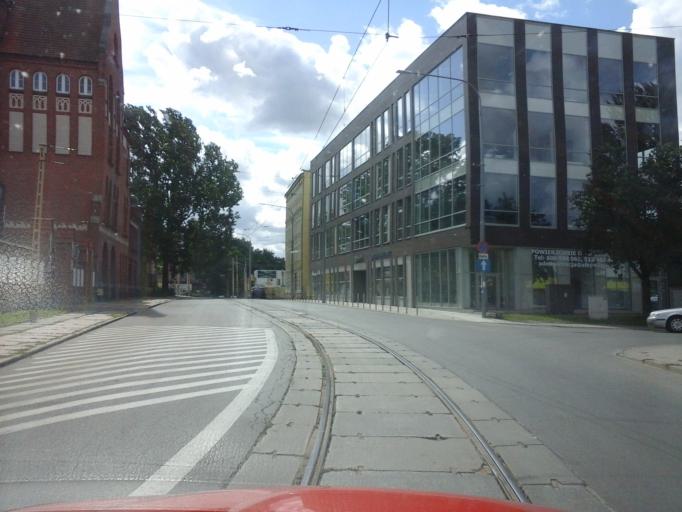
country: PL
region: West Pomeranian Voivodeship
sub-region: Szczecin
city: Szczecin
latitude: 53.4413
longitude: 14.5738
